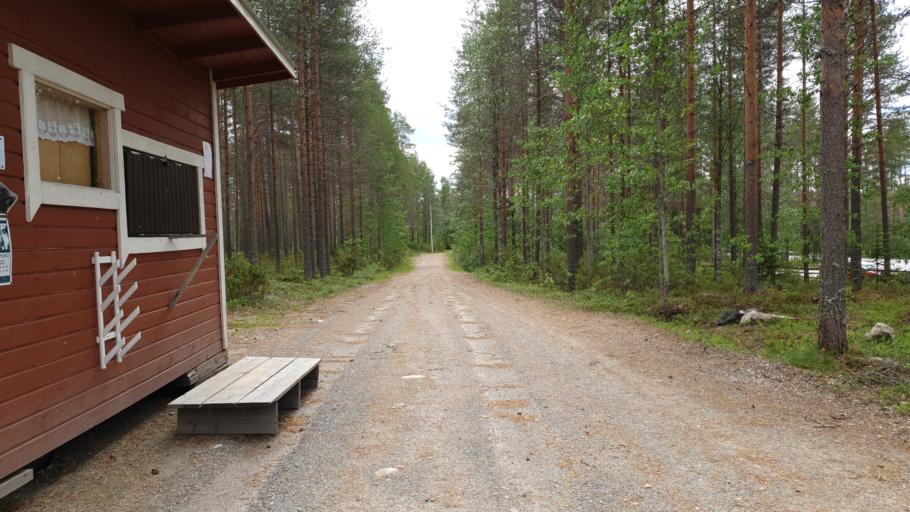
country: FI
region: Kainuu
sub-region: Kehys-Kainuu
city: Kuhmo
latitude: 64.0369
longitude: 29.5767
